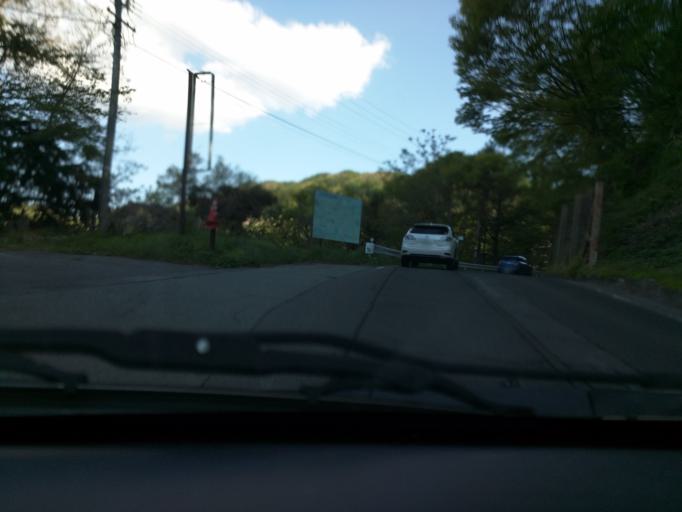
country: JP
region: Nagano
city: Nagano-shi
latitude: 36.6766
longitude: 138.1728
